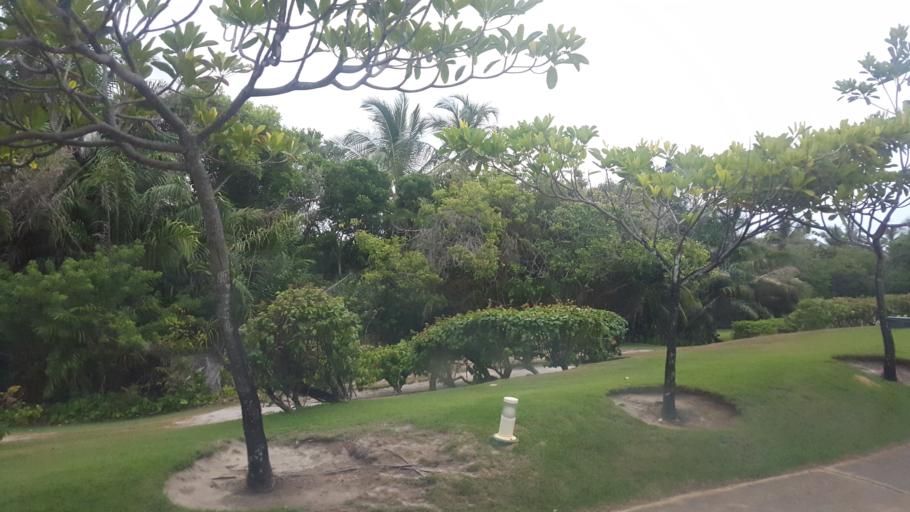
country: BR
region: Bahia
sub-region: Mata De Sao Joao
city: Mata de Sao Joao
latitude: -12.4426
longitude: -37.9235
